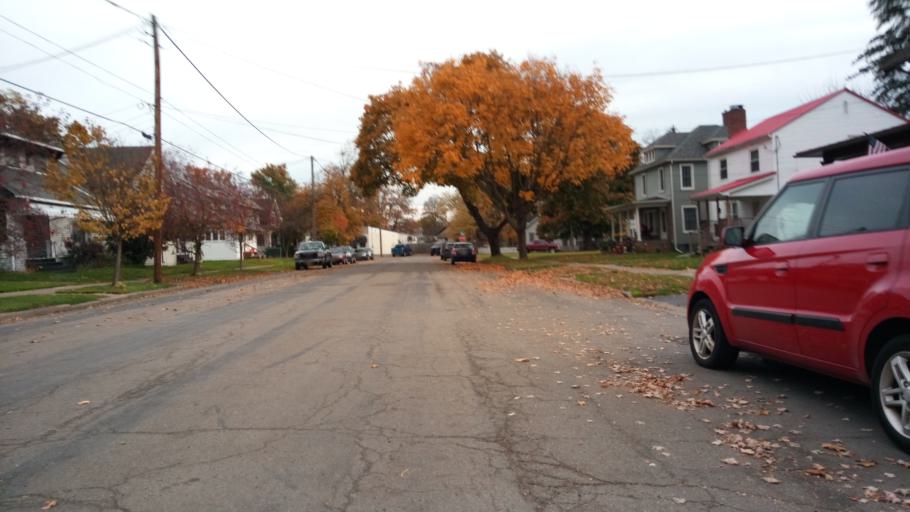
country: US
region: New York
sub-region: Chemung County
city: Elmira
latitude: 42.0806
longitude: -76.7902
